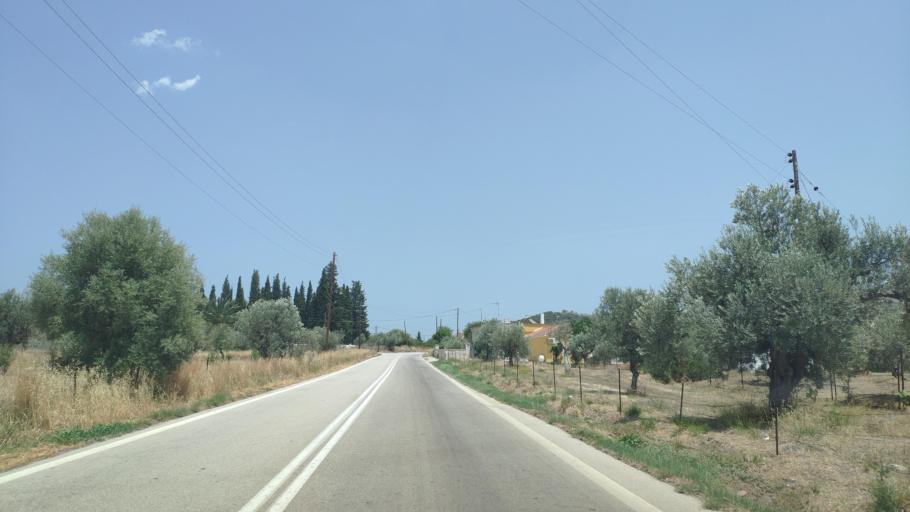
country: GR
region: Peloponnese
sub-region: Nomos Argolidos
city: Didyma
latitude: 37.4315
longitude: 23.1714
